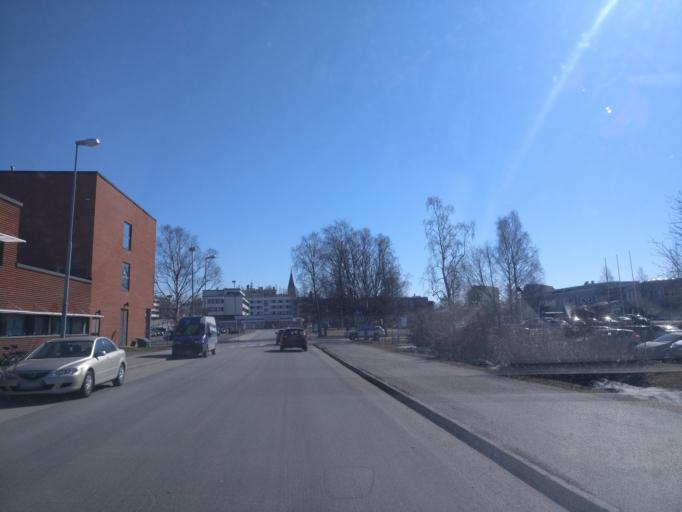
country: FI
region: Lapland
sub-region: Kemi-Tornio
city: Kemi
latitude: 65.7356
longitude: 24.5563
